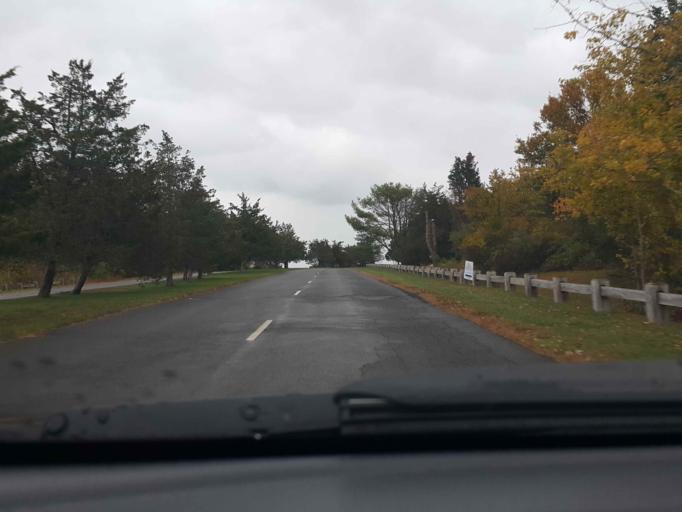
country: US
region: Connecticut
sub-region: Middlesex County
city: Clinton
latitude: 41.2677
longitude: -72.5550
